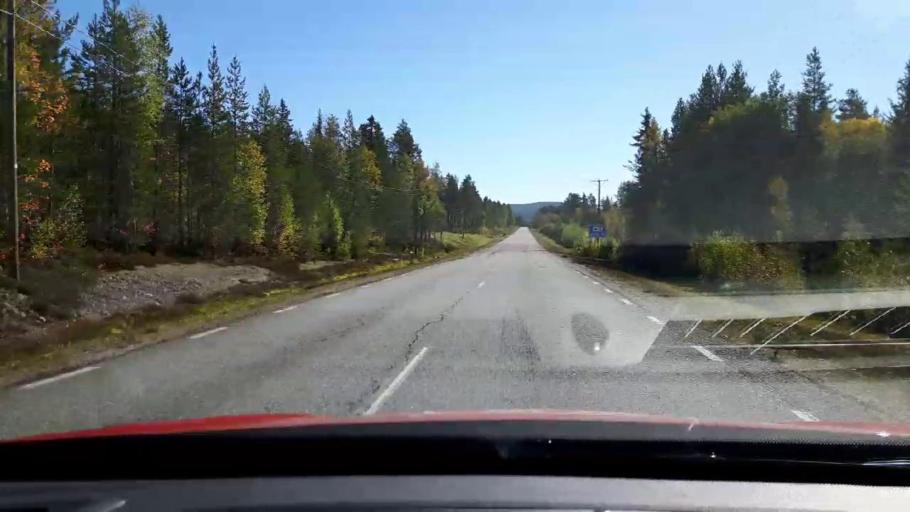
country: SE
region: Jaemtland
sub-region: Harjedalens Kommun
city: Sveg
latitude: 62.3017
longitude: 14.0614
